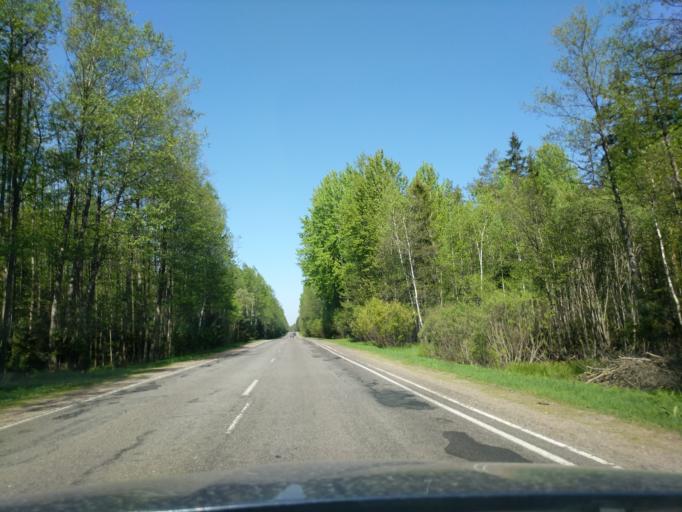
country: BY
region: Minsk
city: Il'ya
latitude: 54.4023
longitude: 27.3244
